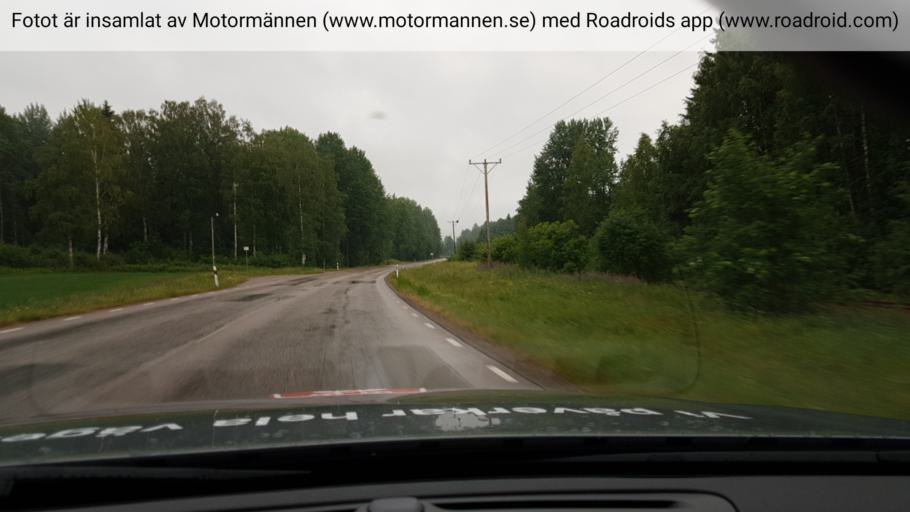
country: SE
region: Vaestmanland
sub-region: Norbergs Kommun
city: Norberg
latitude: 60.0416
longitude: 15.9623
